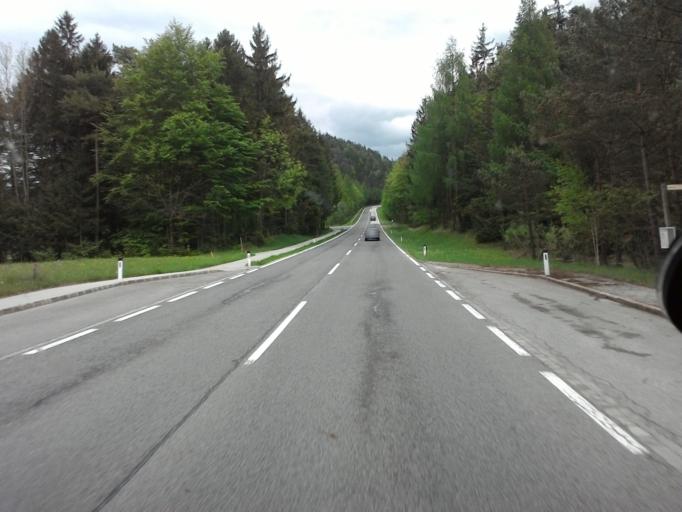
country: AT
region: Upper Austria
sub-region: Politischer Bezirk Kirchdorf an der Krems
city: Rossleithen
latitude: 47.7588
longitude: 14.2170
